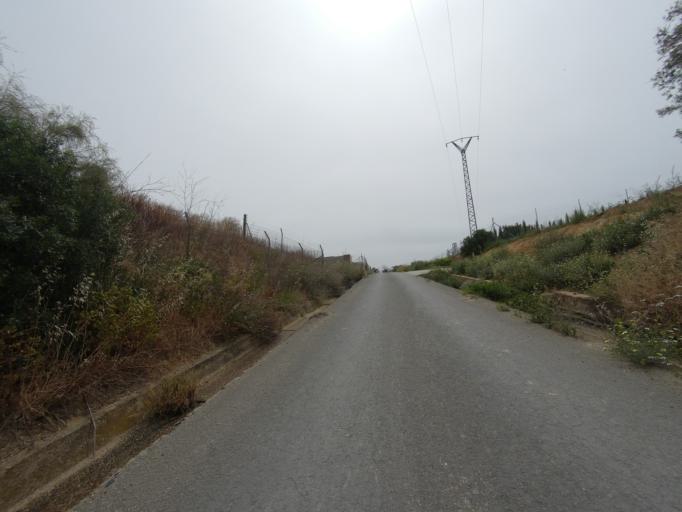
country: ES
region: Andalusia
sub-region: Provincia de Huelva
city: Palos de la Frontera
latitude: 37.2428
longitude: -6.8860
